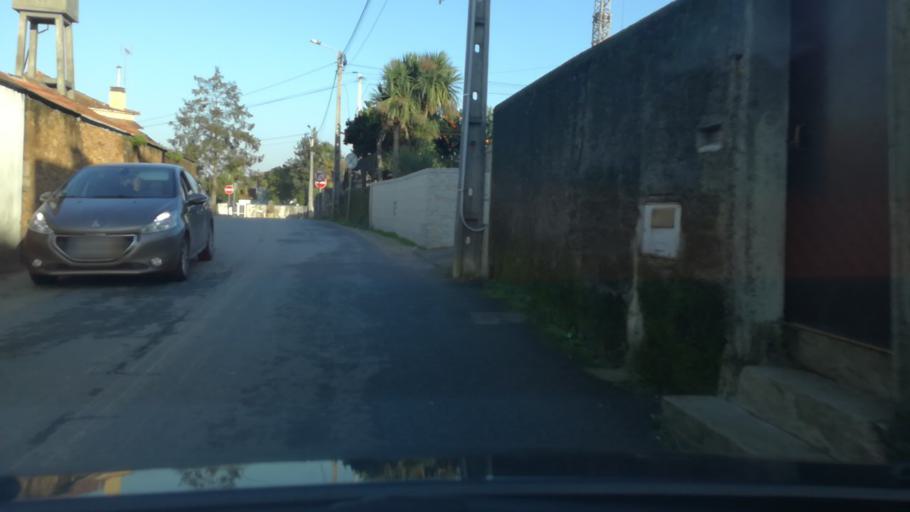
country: PT
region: Braga
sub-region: Vila Nova de Famalicao
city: Ferreiros
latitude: 41.3495
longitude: -8.5252
